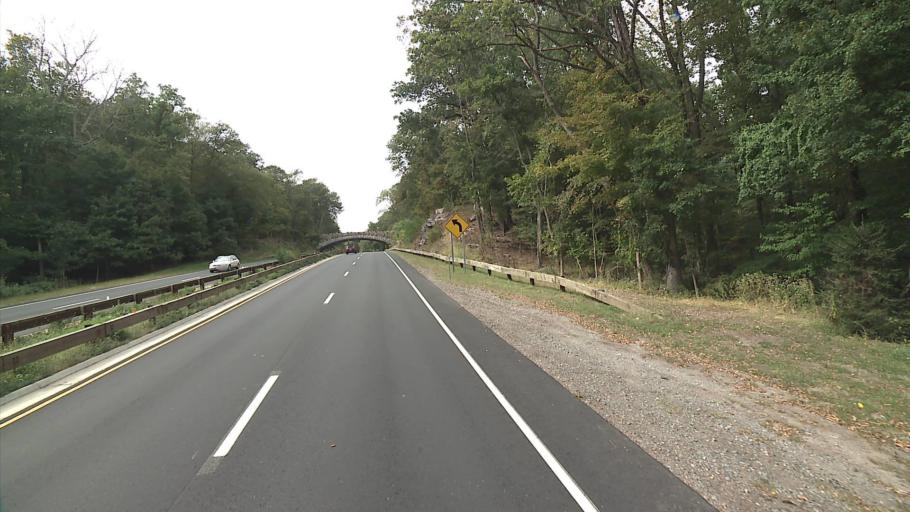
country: US
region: Connecticut
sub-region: Fairfield County
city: North Stamford
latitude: 41.1008
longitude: -73.5902
